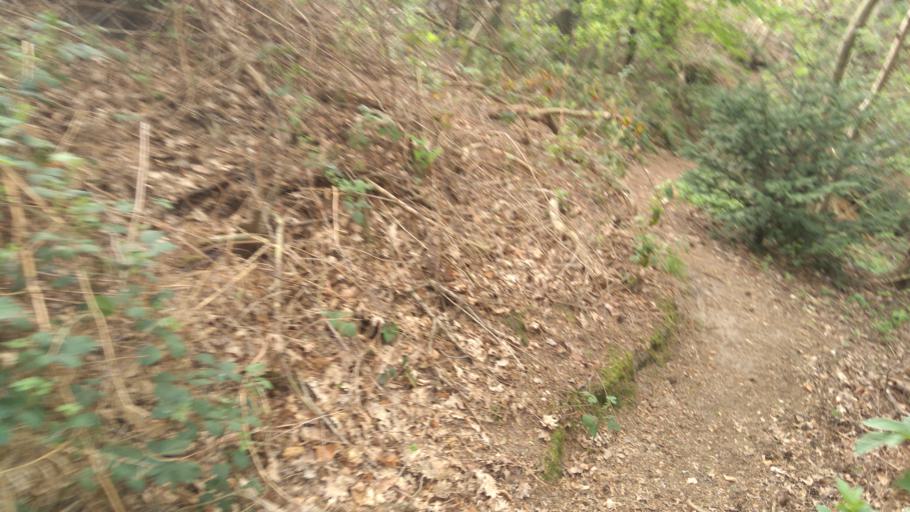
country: DE
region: Lower Saxony
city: Buxtehude
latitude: 53.4628
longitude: 9.6531
